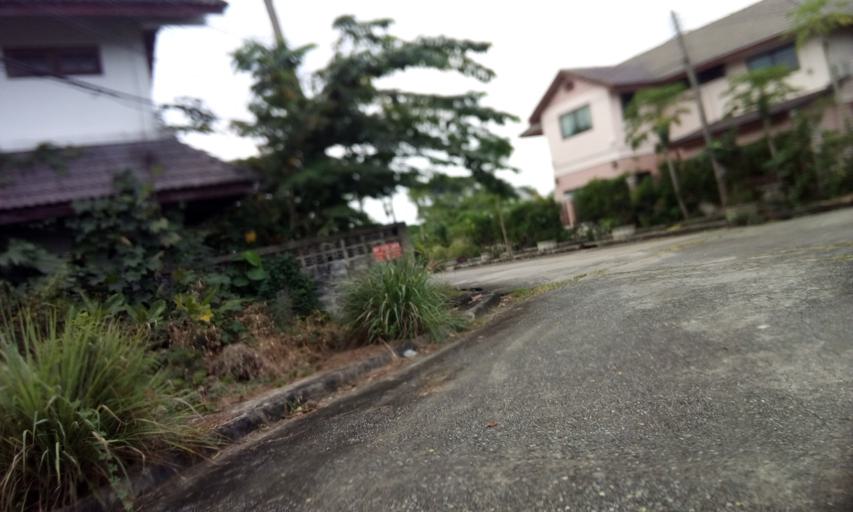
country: TH
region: Pathum Thani
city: Nong Suea
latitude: 14.0619
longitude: 100.8784
